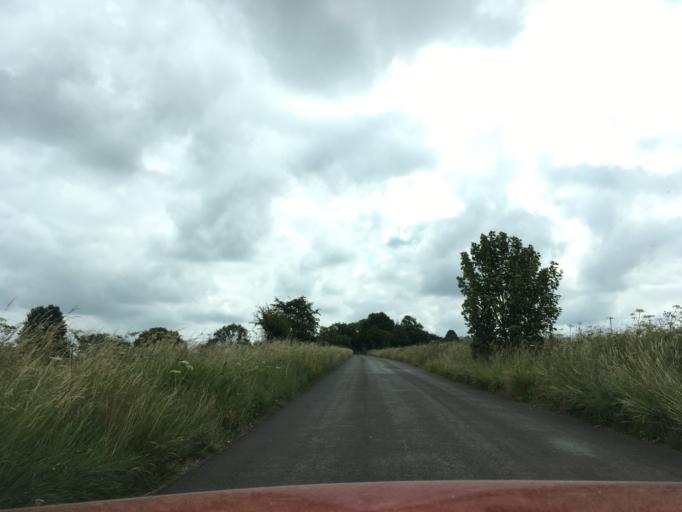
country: GB
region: England
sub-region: Oxfordshire
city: Chipping Norton
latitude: 51.9277
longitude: -1.5721
